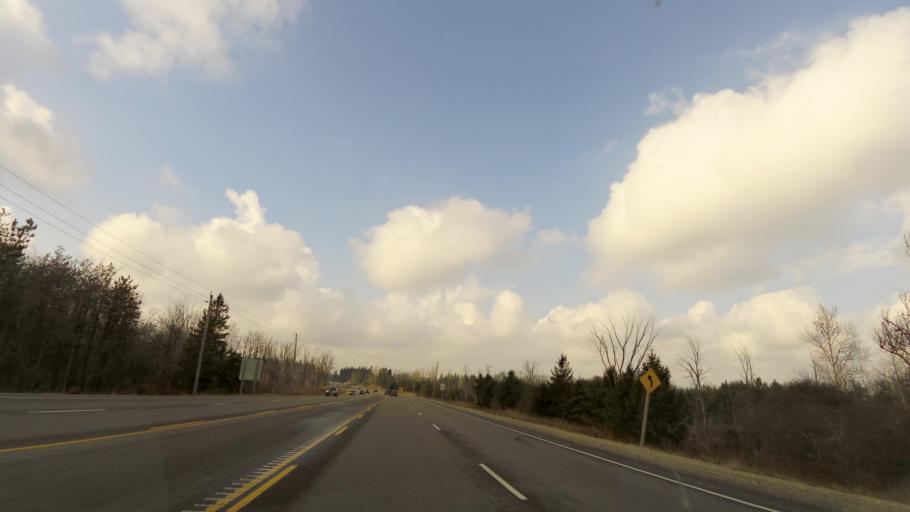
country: CA
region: Ontario
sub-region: Halton
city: Milton
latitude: 43.4212
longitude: -80.0695
